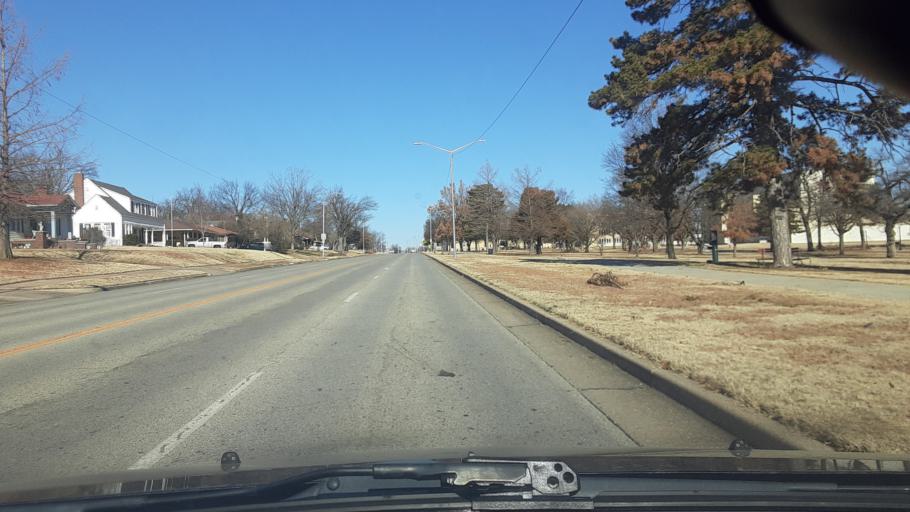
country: US
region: Oklahoma
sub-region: Kay County
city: Ponca City
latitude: 36.7118
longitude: -97.0783
